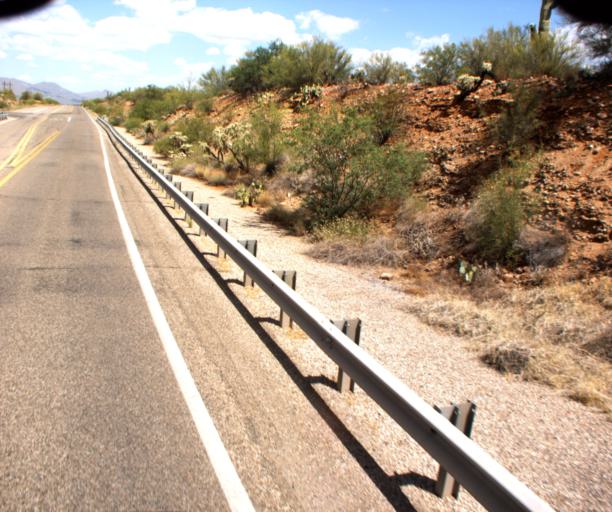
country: US
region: Arizona
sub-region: Pinal County
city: Kearny
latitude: 33.0626
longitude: -110.9080
